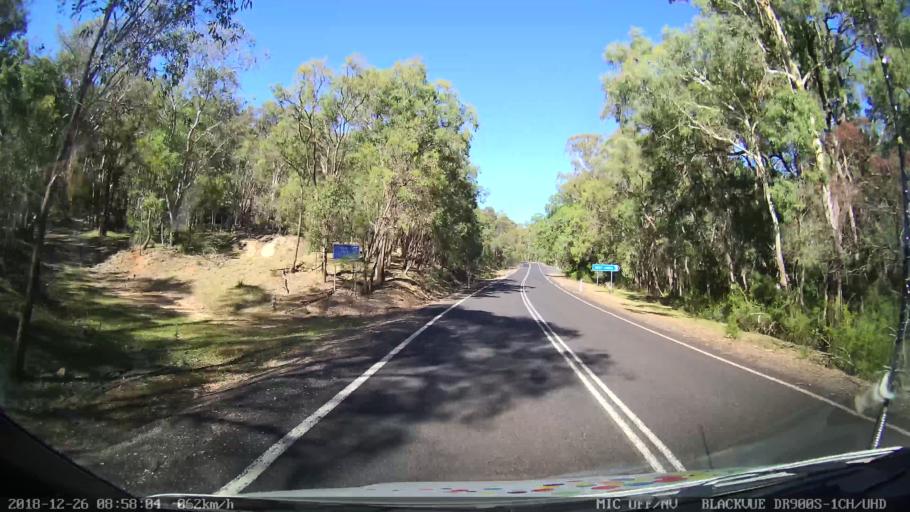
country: AU
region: New South Wales
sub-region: Mid-Western Regional
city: Kandos
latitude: -32.6271
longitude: 150.0464
